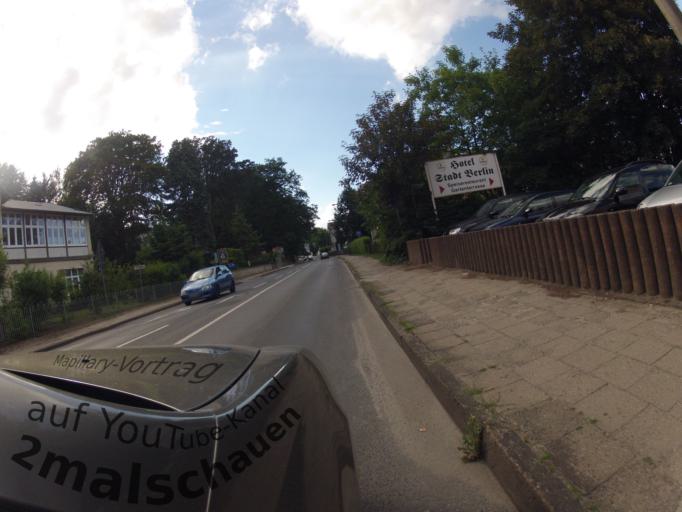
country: DE
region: Mecklenburg-Vorpommern
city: Seebad Heringsdorf
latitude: 53.9514
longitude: 14.1671
